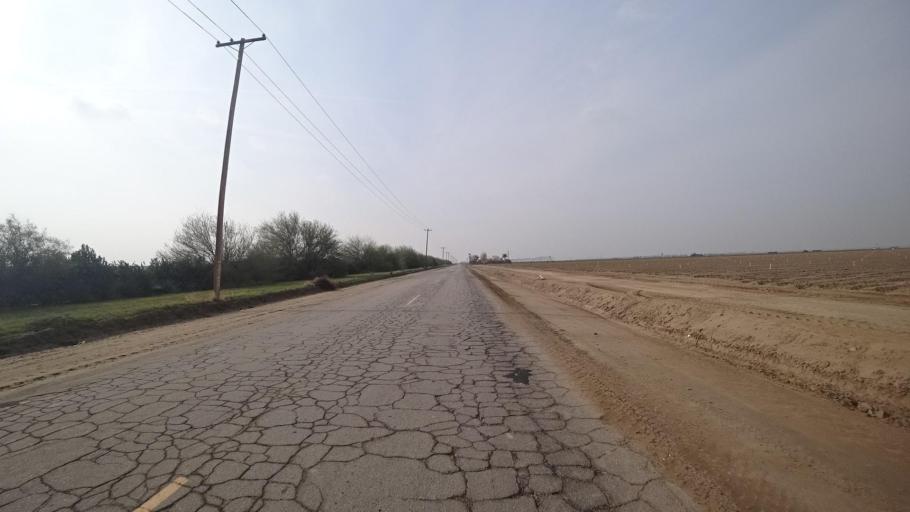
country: US
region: California
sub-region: Kern County
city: Arvin
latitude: 35.1507
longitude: -118.8842
